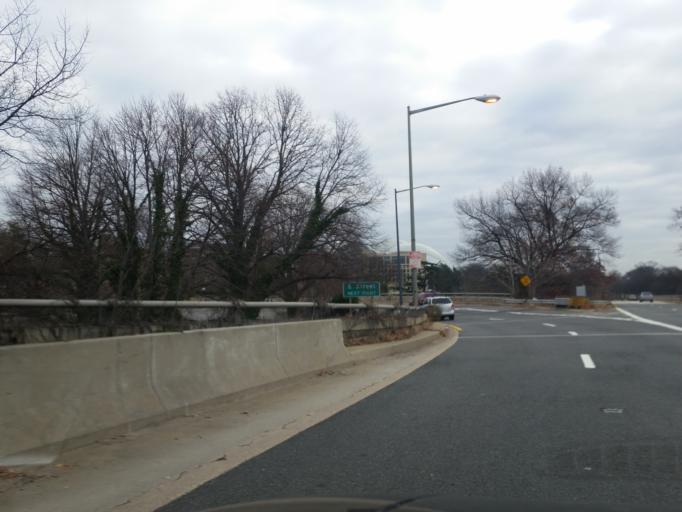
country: US
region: Washington, D.C.
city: Washington, D.C.
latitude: 38.8929
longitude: -77.0546
